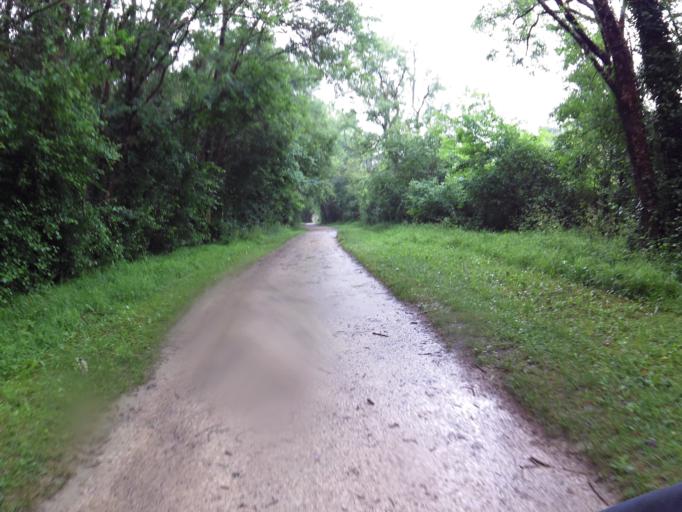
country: FR
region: Poitou-Charentes
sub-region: Departement de la Charente
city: Gond-Pontouvre
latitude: 45.6767
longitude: 0.1538
